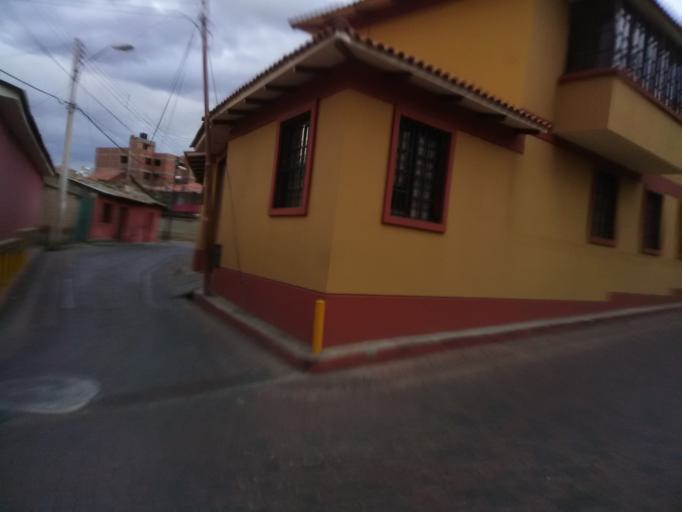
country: BO
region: Cochabamba
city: Cochabamba
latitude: -17.3752
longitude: -66.1415
